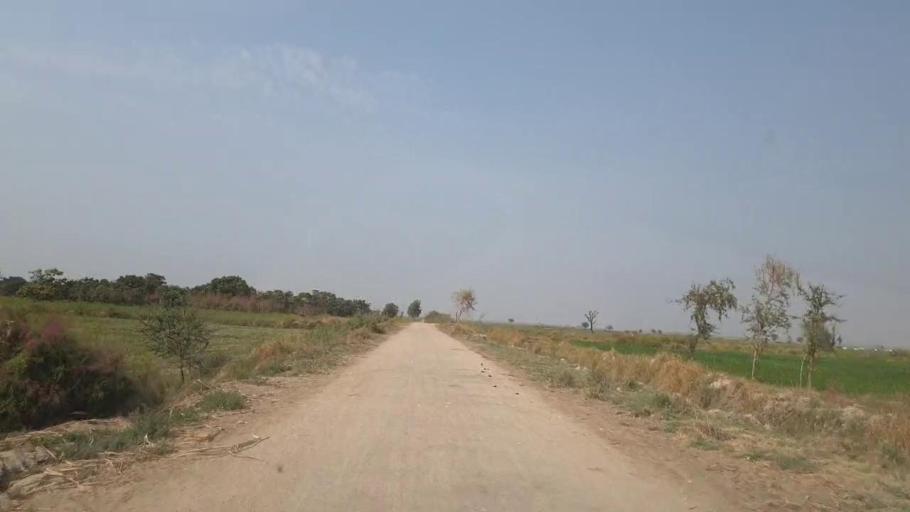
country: PK
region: Sindh
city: Mirpur Khas
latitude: 25.5834
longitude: 69.1364
